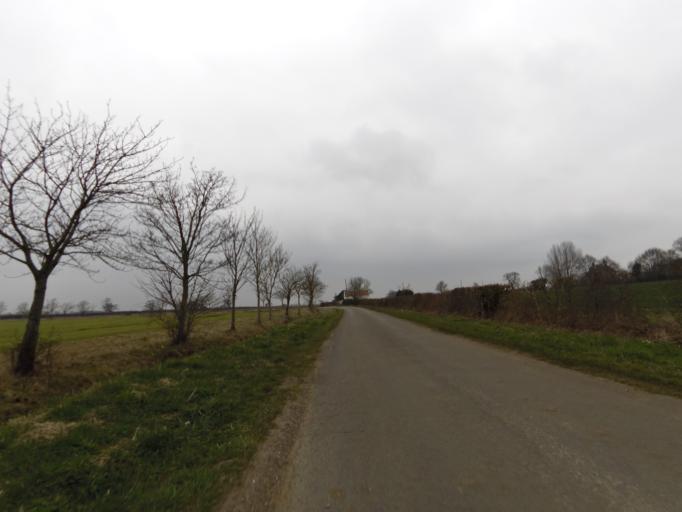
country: GB
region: England
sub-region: Suffolk
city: Framlingham
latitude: 52.2349
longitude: 1.3763
